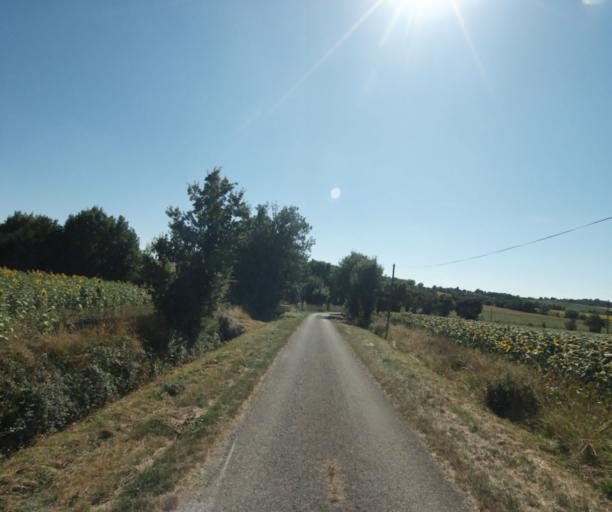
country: FR
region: Midi-Pyrenees
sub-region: Departement de la Haute-Garonne
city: Saint-Felix-Lauragais
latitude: 43.4979
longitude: 1.9097
